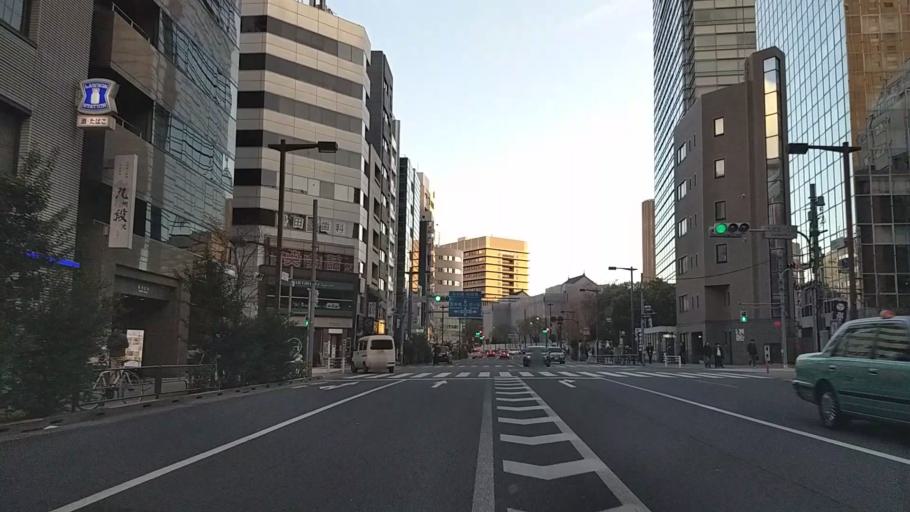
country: JP
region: Tokyo
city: Tokyo
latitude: 35.6972
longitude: 139.7507
